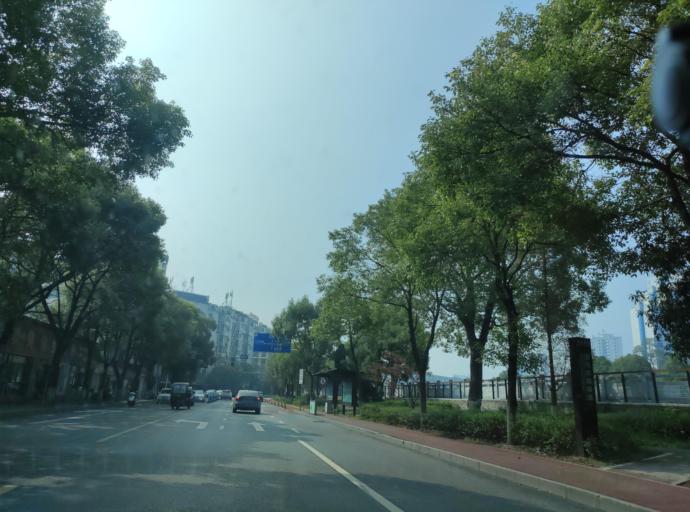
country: CN
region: Jiangxi Sheng
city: Pingxiang
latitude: 27.6382
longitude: 113.8544
